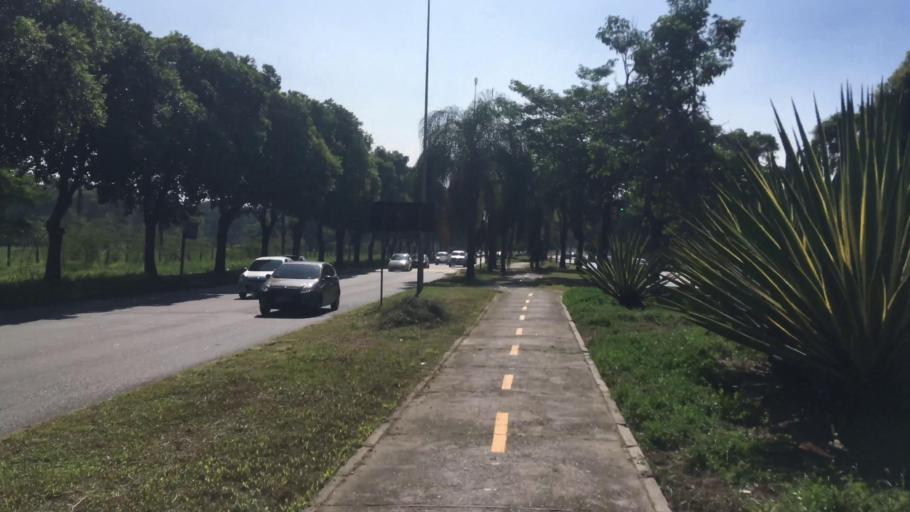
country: BR
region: Rio de Janeiro
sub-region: Rio De Janeiro
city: Rio de Janeiro
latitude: -22.8503
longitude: -43.2347
